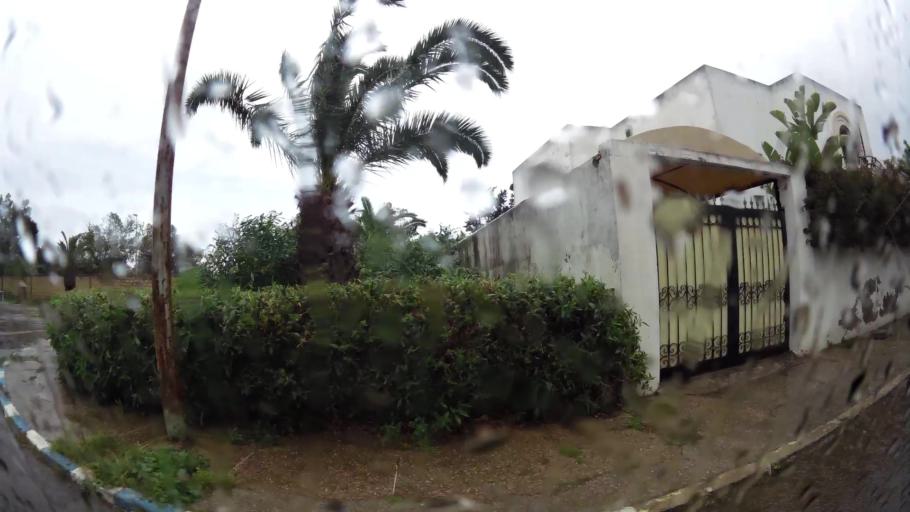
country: MA
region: Grand Casablanca
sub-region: Casablanca
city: Casablanca
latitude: 33.5718
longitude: -7.6335
